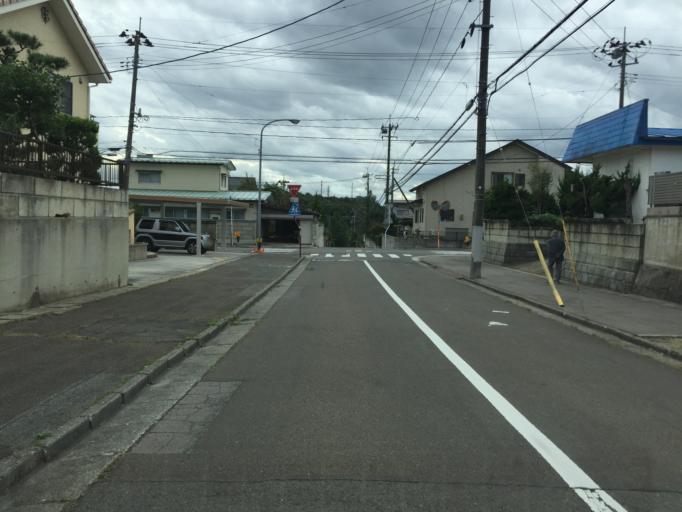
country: JP
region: Fukushima
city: Fukushima-shi
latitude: 37.6948
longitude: 140.4777
